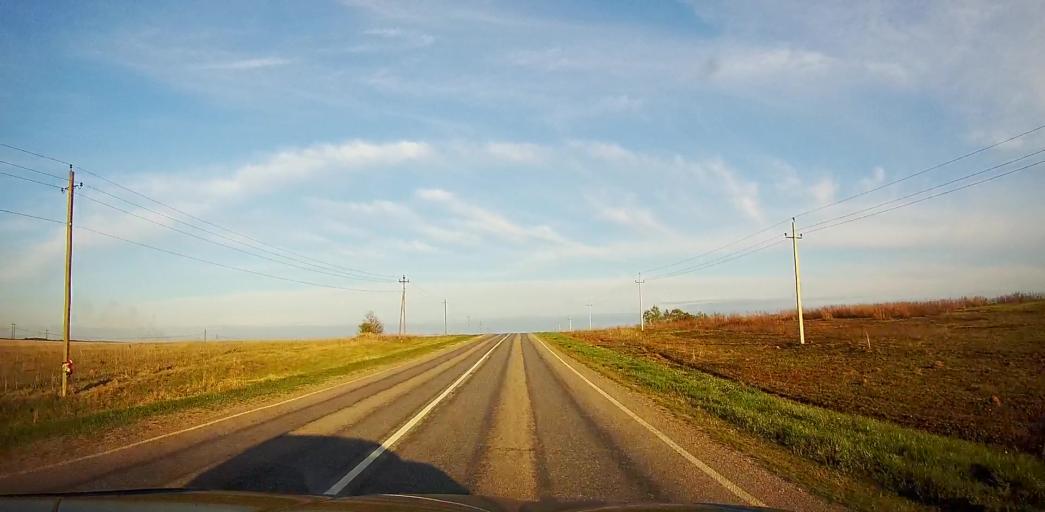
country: RU
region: Moskovskaya
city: Meshcherino
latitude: 55.2689
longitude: 38.2449
